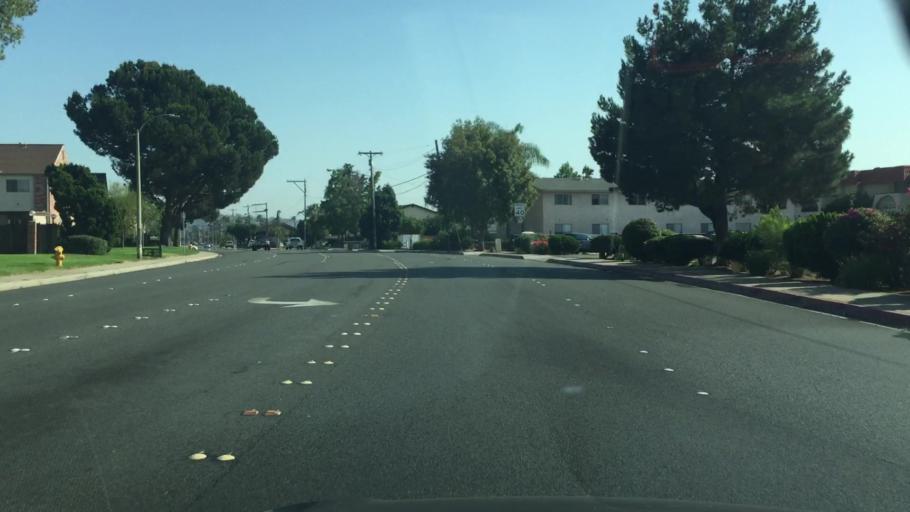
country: US
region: California
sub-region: San Diego County
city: Bostonia
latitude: 32.8131
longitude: -116.9509
